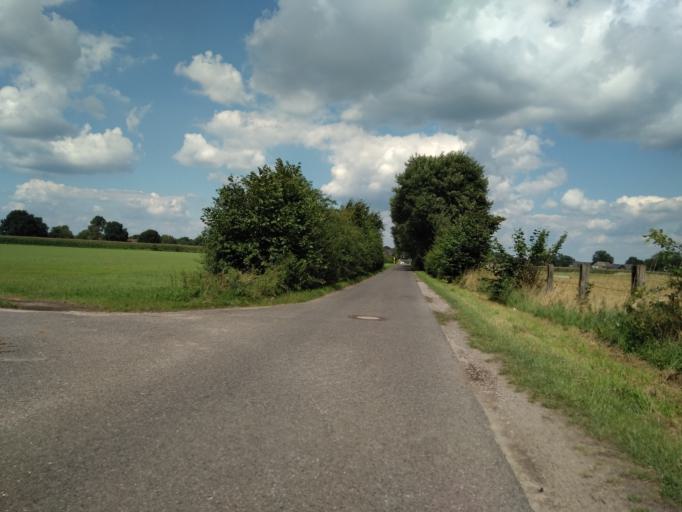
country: DE
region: North Rhine-Westphalia
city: Dorsten
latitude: 51.6420
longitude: 6.9828
